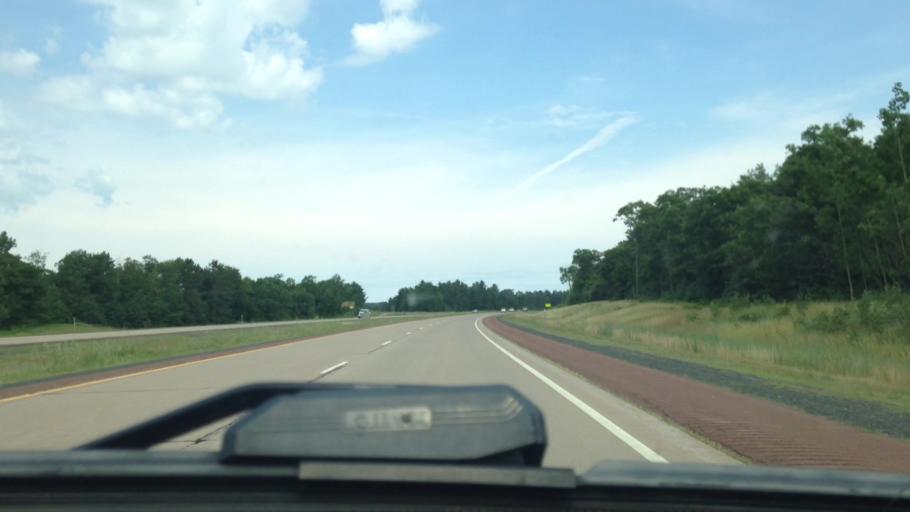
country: US
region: Wisconsin
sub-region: Douglas County
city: Lake Nebagamon
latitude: 46.3366
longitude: -91.8299
